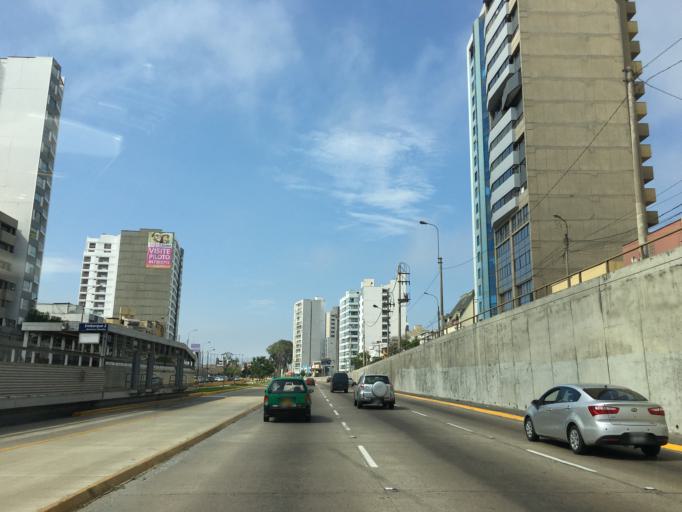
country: PE
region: Lima
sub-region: Lima
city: Surco
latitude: -12.1303
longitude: -77.0225
